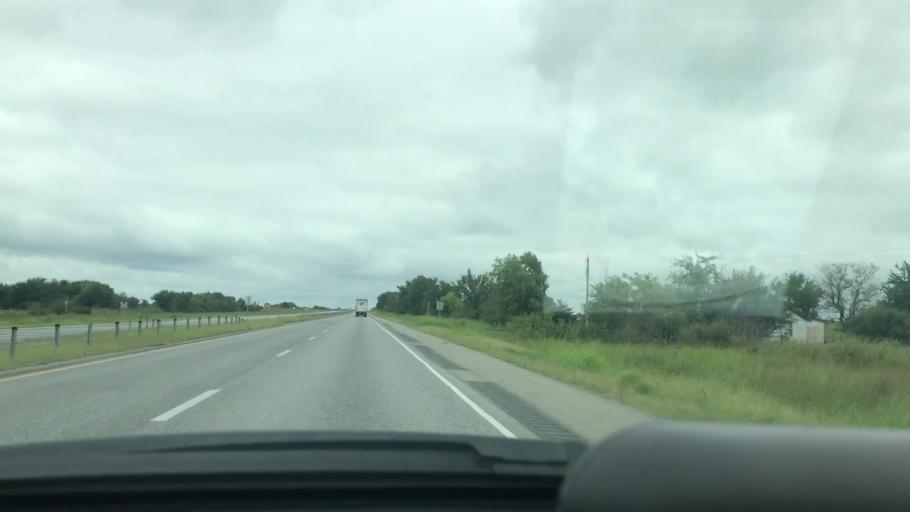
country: US
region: Oklahoma
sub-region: Pittsburg County
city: McAlester
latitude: 34.7456
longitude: -95.8960
